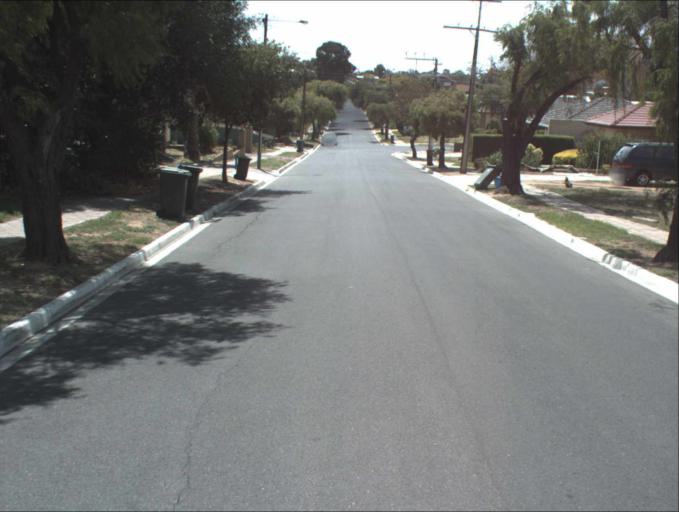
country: AU
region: South Australia
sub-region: Port Adelaide Enfield
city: Gilles Plains
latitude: -34.8444
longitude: 138.6514
